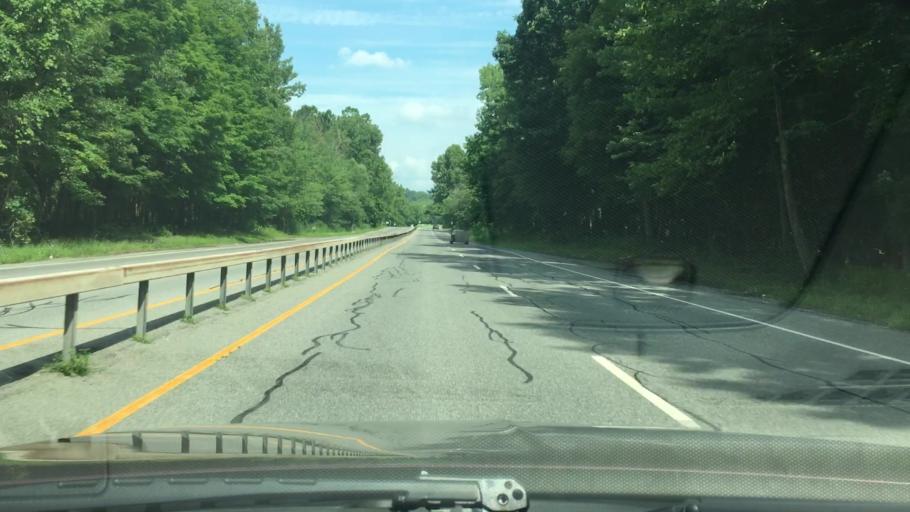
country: US
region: New York
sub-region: Dutchess County
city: Brinckerhoff
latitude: 41.5382
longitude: -73.8129
